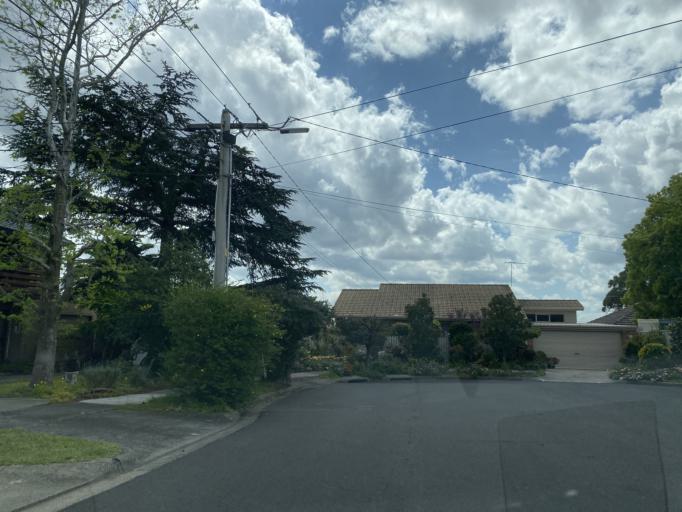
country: AU
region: Victoria
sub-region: Whitehorse
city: Burwood
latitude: -37.8586
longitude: 145.1183
